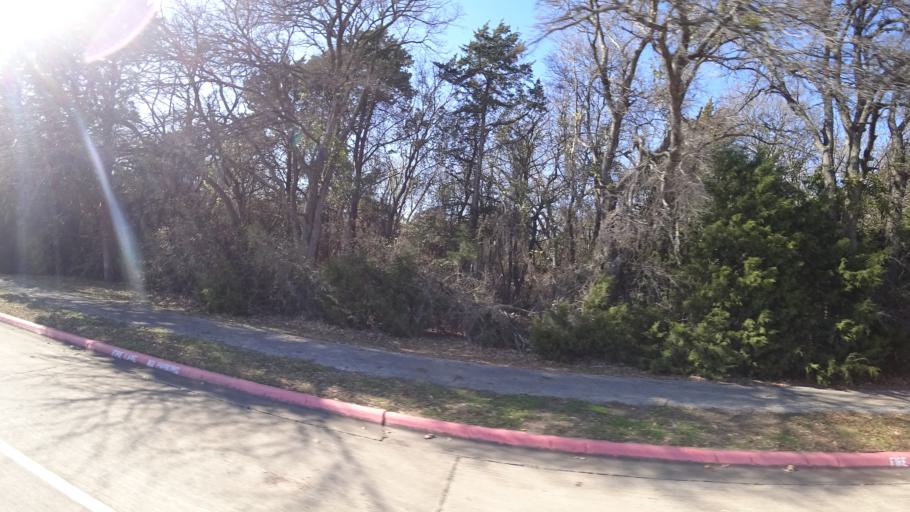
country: US
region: Texas
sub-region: Denton County
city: Lewisville
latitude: 33.0024
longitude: -97.0044
